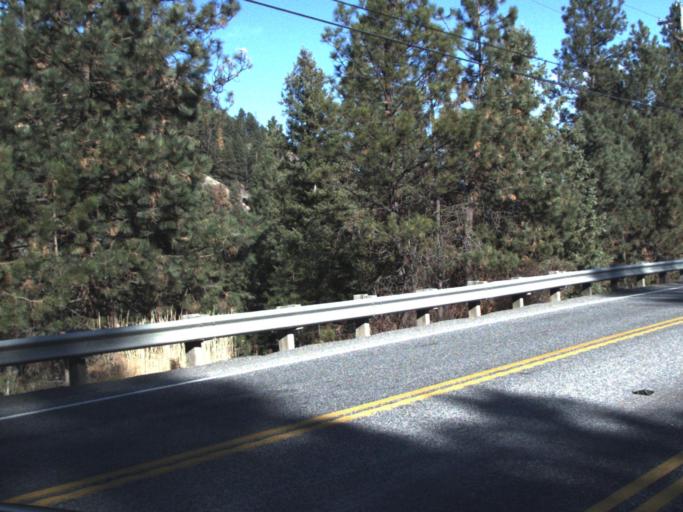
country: US
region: Washington
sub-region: Ferry County
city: Republic
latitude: 48.6535
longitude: -118.6709
